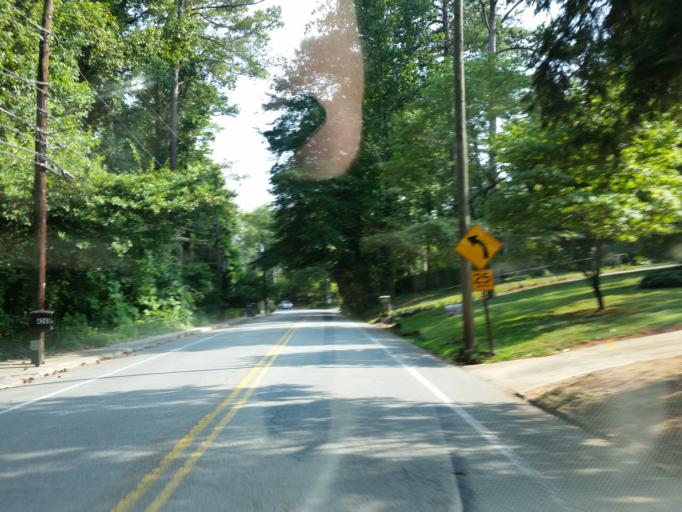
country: US
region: Georgia
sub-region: DeKalb County
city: North Atlanta
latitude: 33.8709
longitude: -84.3584
